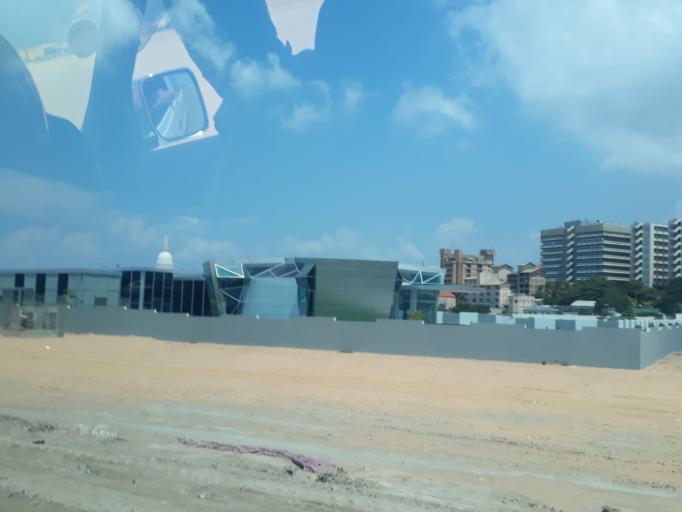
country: LK
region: Western
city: Colombo
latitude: 6.9325
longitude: 79.8387
